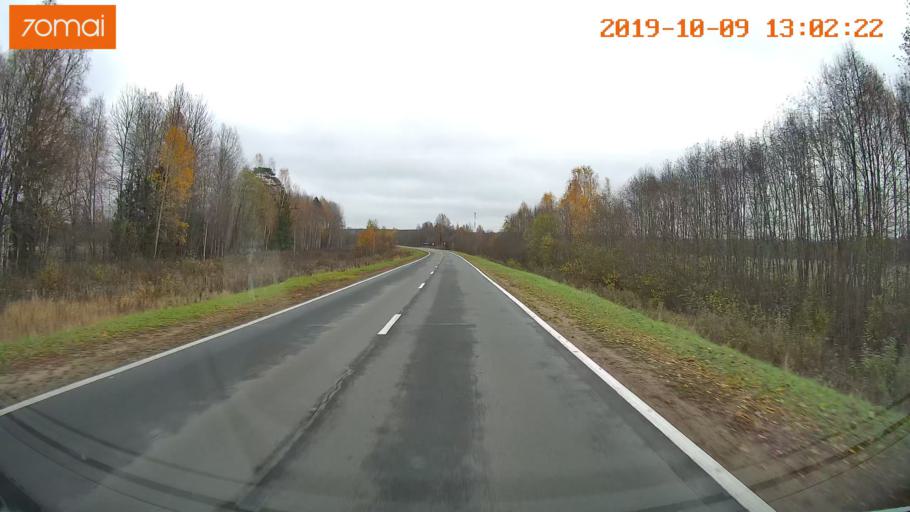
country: RU
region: Jaroslavl
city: Prechistoye
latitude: 58.3618
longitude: 40.4999
